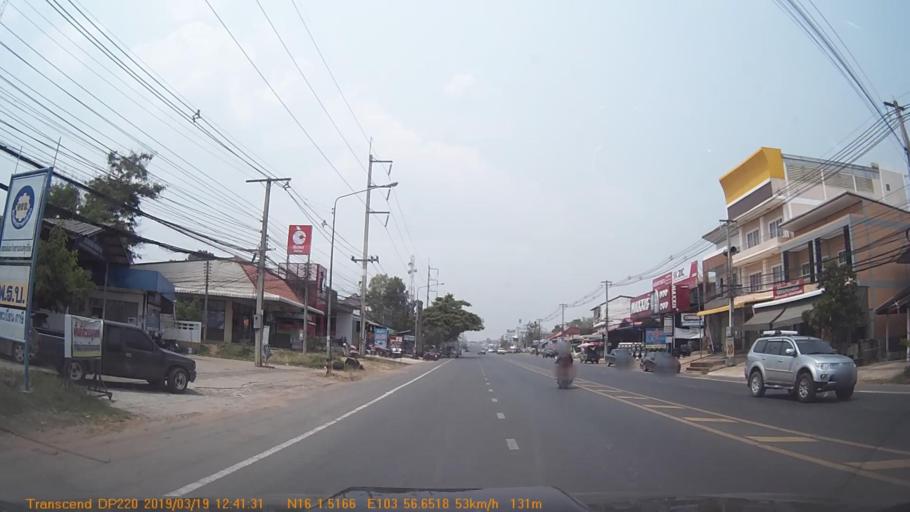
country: TH
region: Roi Et
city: Selaphum
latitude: 16.0254
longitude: 103.9441
